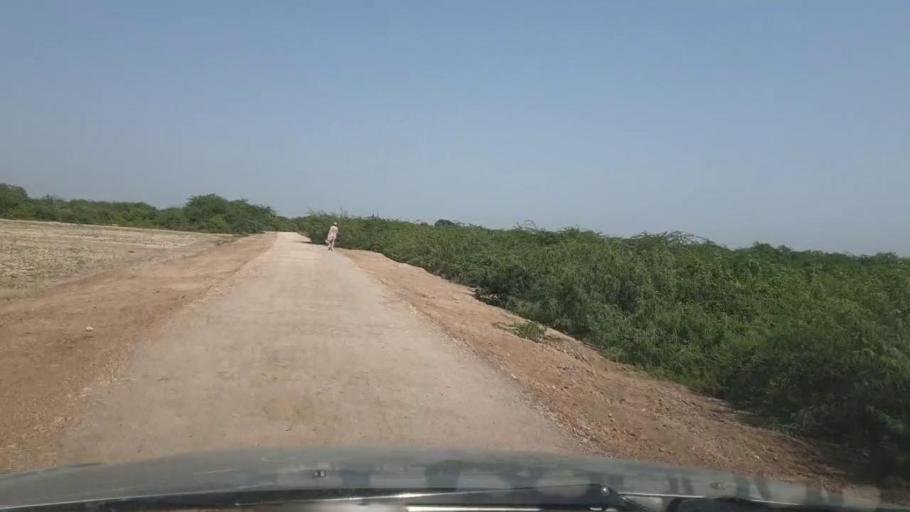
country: PK
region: Sindh
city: Tando Ghulam Ali
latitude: 25.1586
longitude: 68.8823
